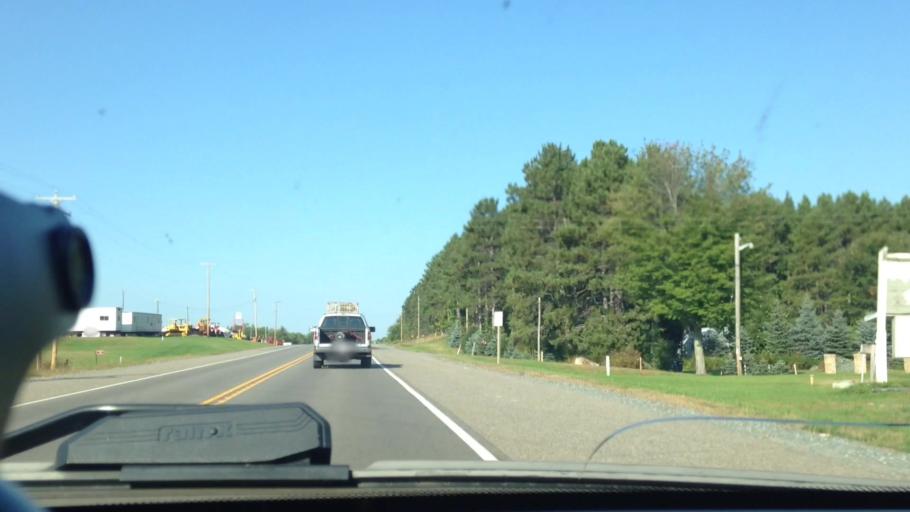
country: US
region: Michigan
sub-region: Dickinson County
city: Iron Mountain
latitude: 45.8761
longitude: -88.0904
